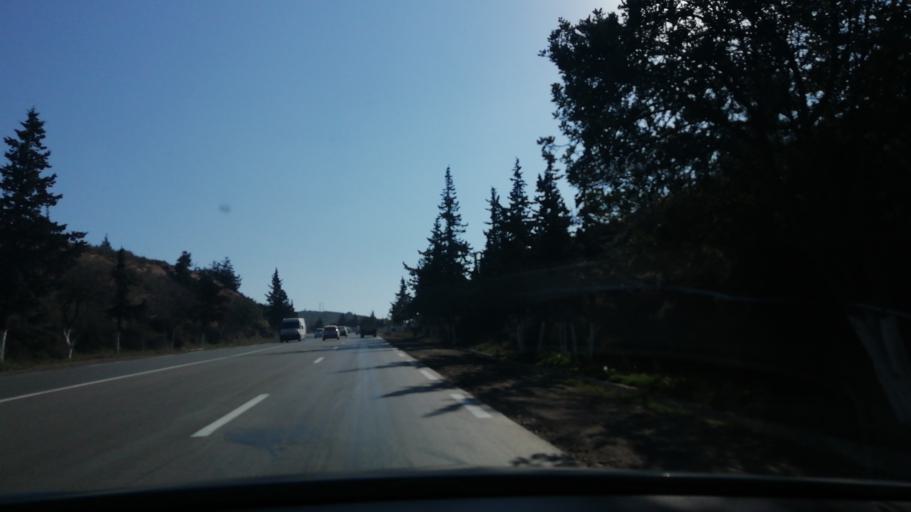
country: DZ
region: Tlemcen
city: Nedroma
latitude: 35.0894
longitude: -1.8187
